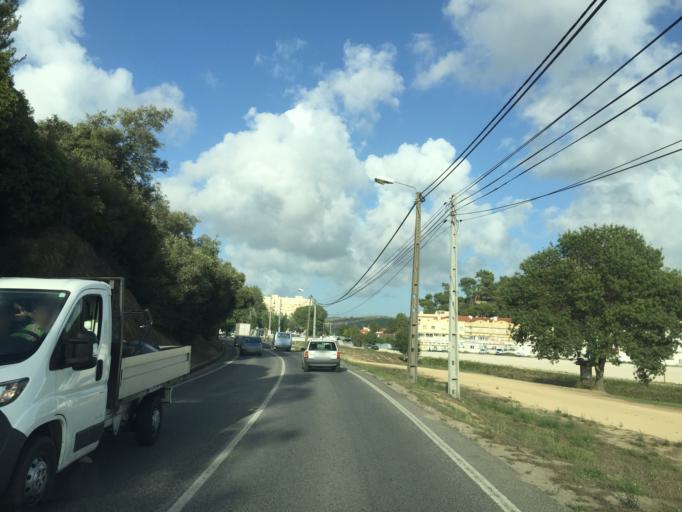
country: PT
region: Lisbon
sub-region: Torres Vedras
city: Torres Vedras
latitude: 39.0959
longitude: -9.2652
